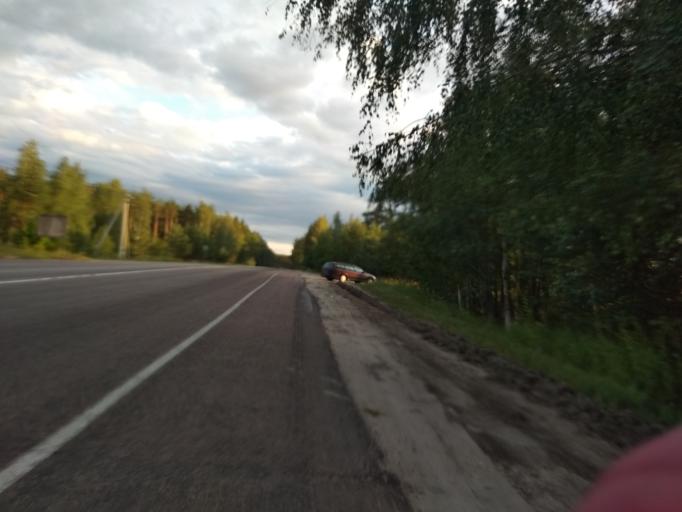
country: RU
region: Moskovskaya
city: Misheronskiy
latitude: 55.6339
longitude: 39.7461
